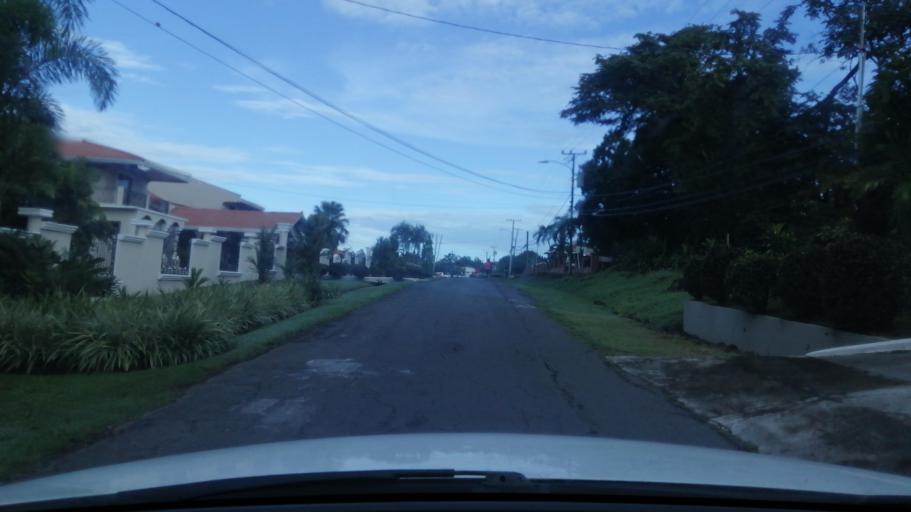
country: PA
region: Chiriqui
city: Mata del Nance
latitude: 8.4582
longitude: -82.4156
